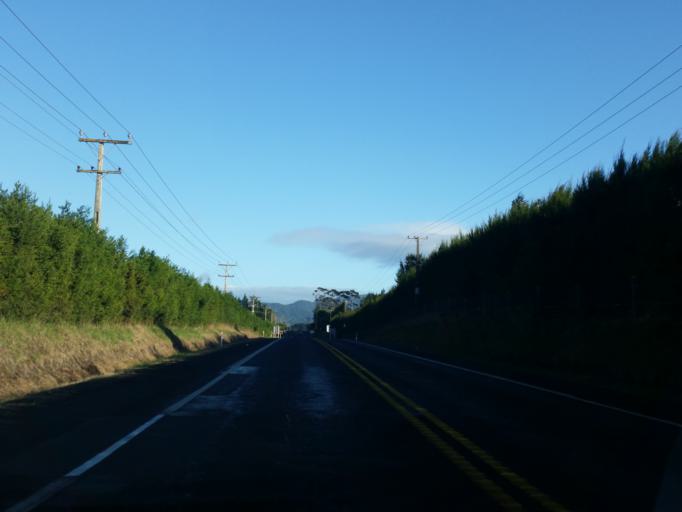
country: NZ
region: Bay of Plenty
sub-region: Western Bay of Plenty District
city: Katikati
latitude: -37.6034
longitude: 175.9315
